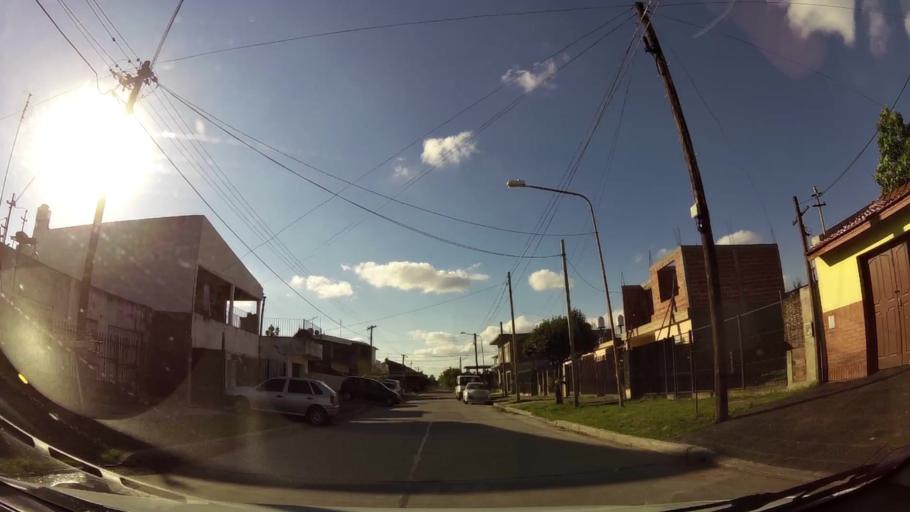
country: AR
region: Buenos Aires
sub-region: Partido de Moron
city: Moron
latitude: -34.6797
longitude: -58.6075
